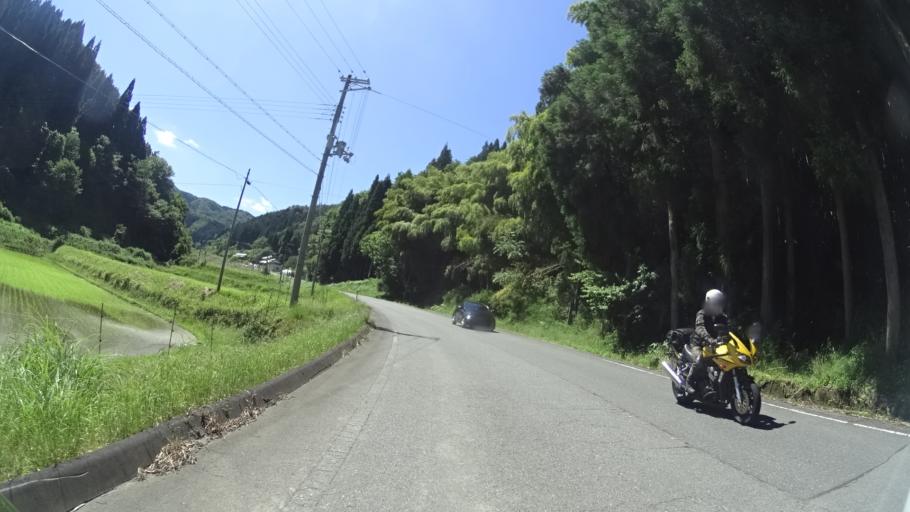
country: JP
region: Kyoto
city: Fukuchiyama
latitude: 35.4233
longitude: 135.0670
